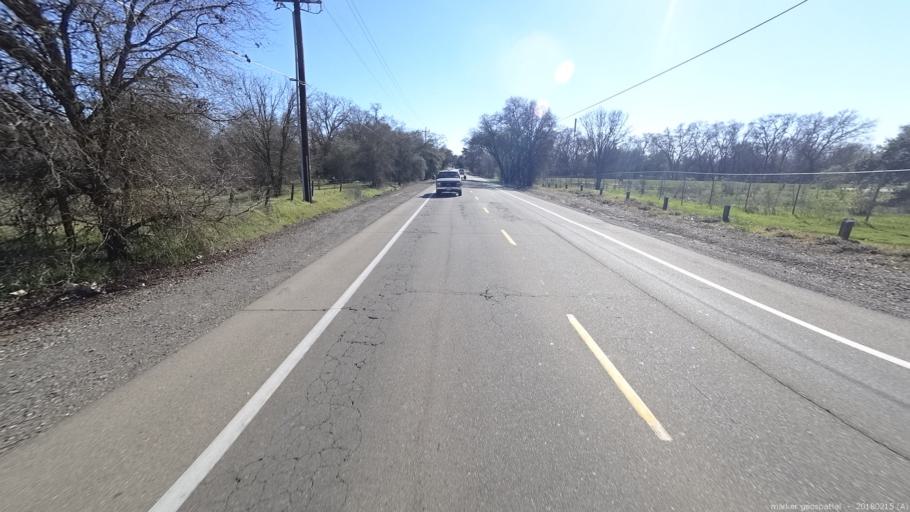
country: US
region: California
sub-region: Sacramento County
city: North Highlands
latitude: 38.7075
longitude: -121.4015
